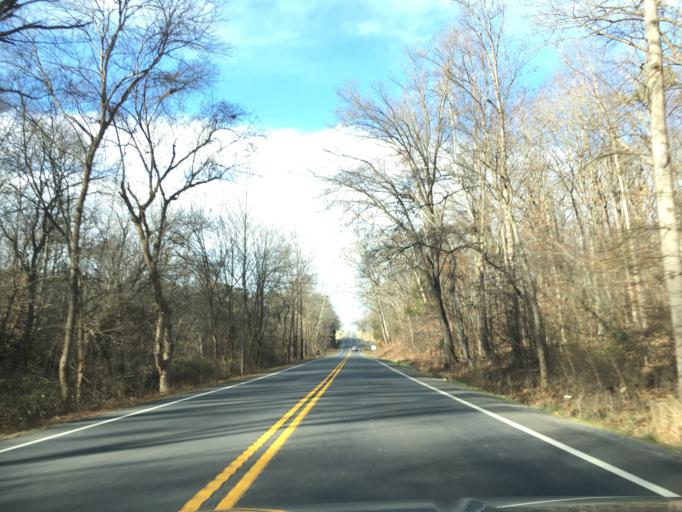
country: US
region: Virginia
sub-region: Culpeper County
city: Culpeper
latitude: 38.3473
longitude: -77.9588
